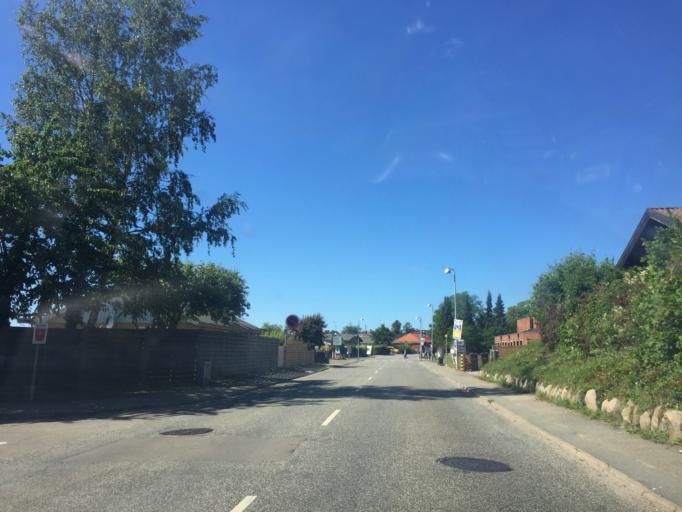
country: DK
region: Capital Region
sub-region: Gribskov Kommune
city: Helsinge
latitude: 56.0185
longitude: 12.1974
